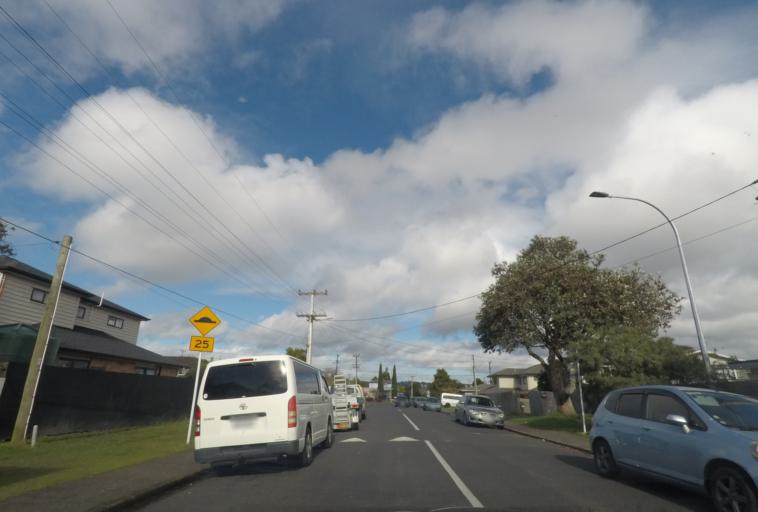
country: NZ
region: Auckland
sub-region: Auckland
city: Waitakere
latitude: -36.8990
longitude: 174.6640
